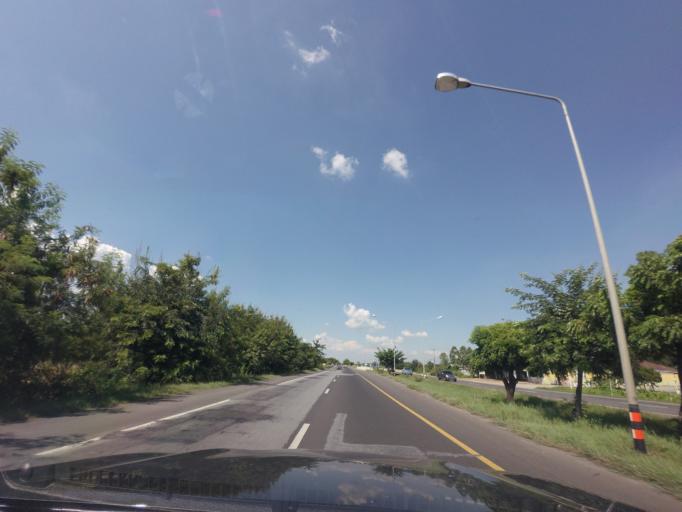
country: TH
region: Nakhon Ratchasima
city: Non Sung
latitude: 15.1984
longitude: 102.3508
